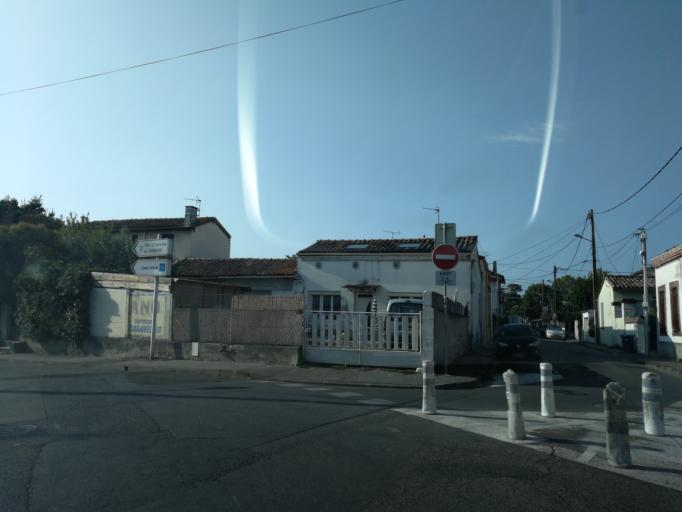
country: FR
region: Midi-Pyrenees
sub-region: Departement de la Haute-Garonne
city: Toulouse
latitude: 43.6267
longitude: 1.4305
